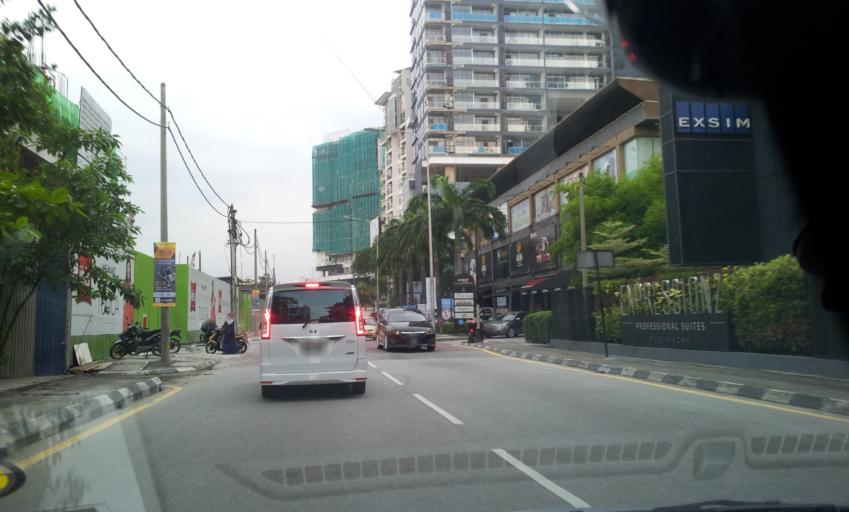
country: MY
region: Kuala Lumpur
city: Kuala Lumpur
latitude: 3.1627
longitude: 101.7142
